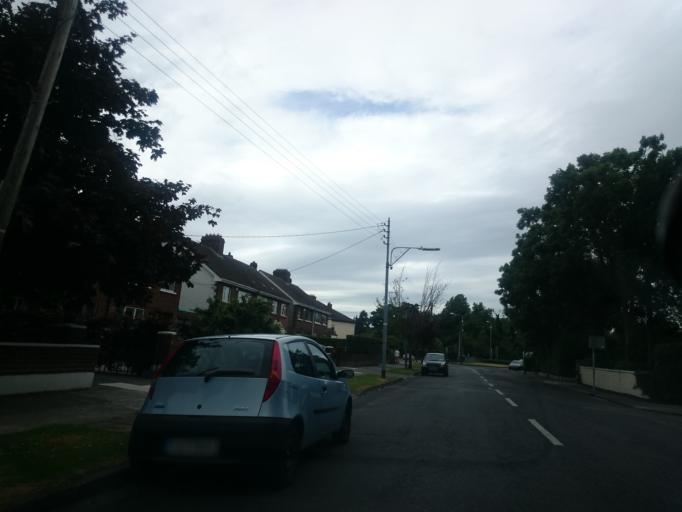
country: IE
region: Leinster
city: Templeogue
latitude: 53.3091
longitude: -6.3024
